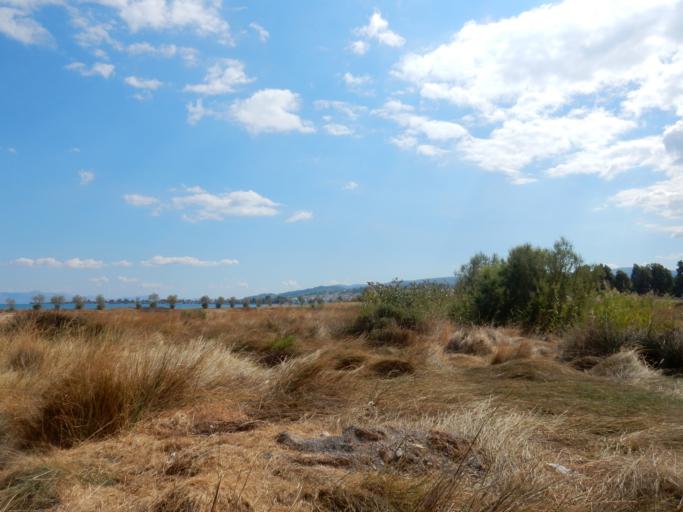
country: GR
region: Attica
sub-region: Nomarchia Anatolikis Attikis
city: Skala Oropou
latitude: 38.3264
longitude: 23.7786
